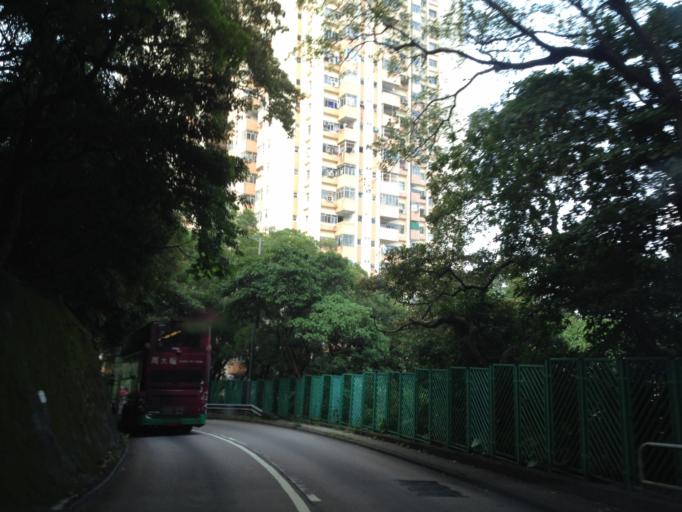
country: HK
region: Wanchai
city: Wan Chai
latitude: 22.2668
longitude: 114.2321
